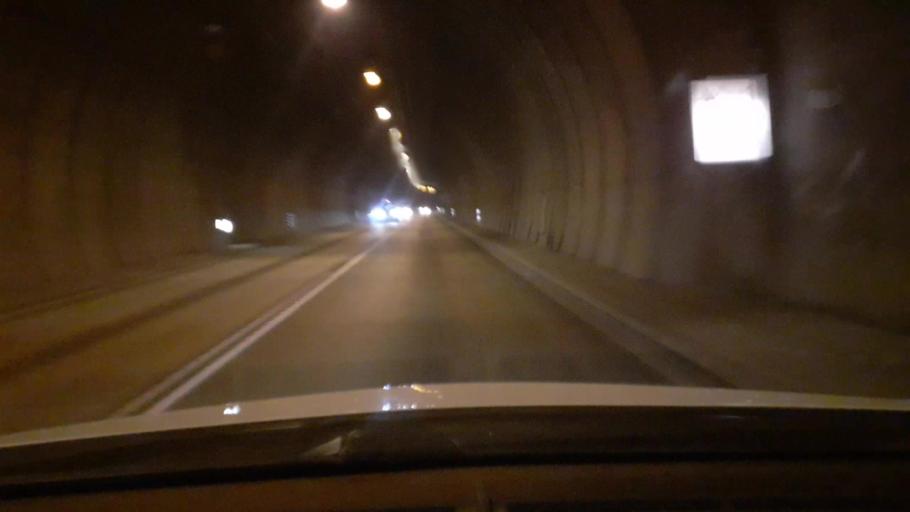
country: IS
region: Capital Region
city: Reykjavik
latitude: 64.2869
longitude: -21.8504
